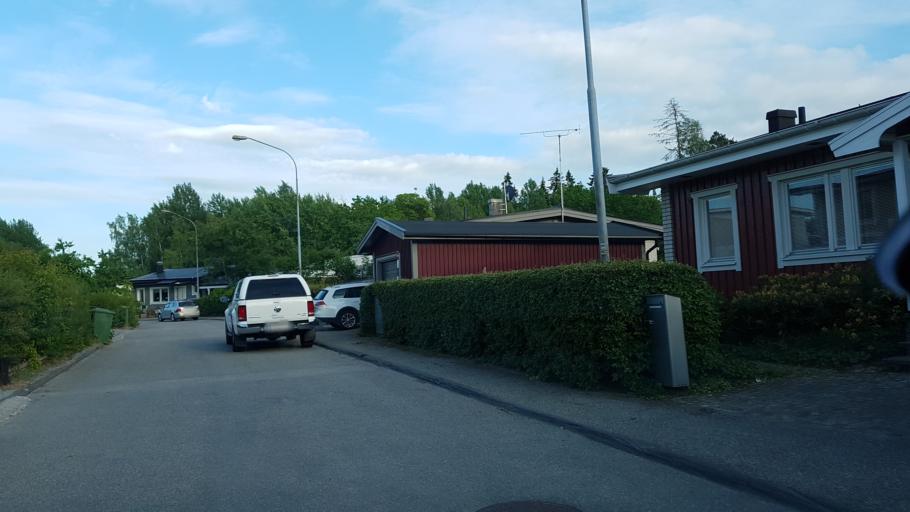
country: SE
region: Stockholm
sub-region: Salems Kommun
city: Ronninge
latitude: 59.2017
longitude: 17.7480
